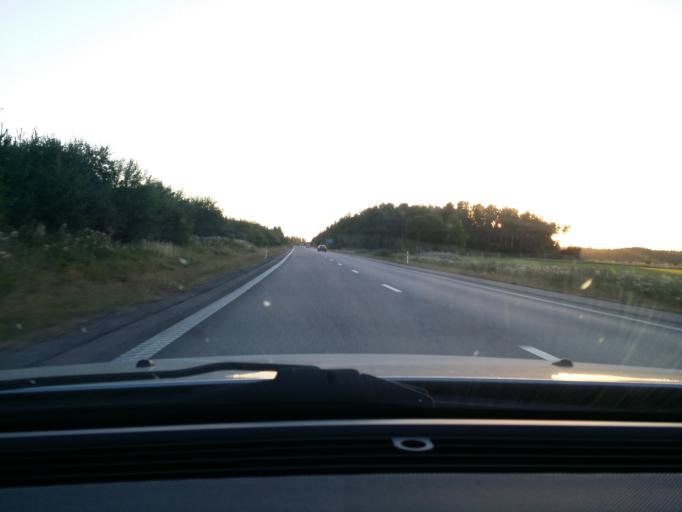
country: SE
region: Uppsala
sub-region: Enkopings Kommun
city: Grillby
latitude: 59.6458
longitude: 17.1771
